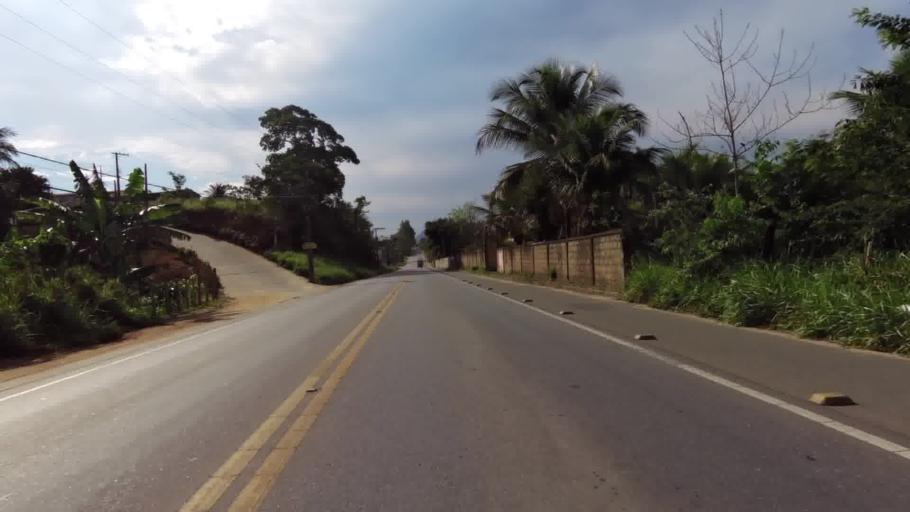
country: BR
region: Espirito Santo
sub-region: Piuma
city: Piuma
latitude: -20.8267
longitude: -40.7314
